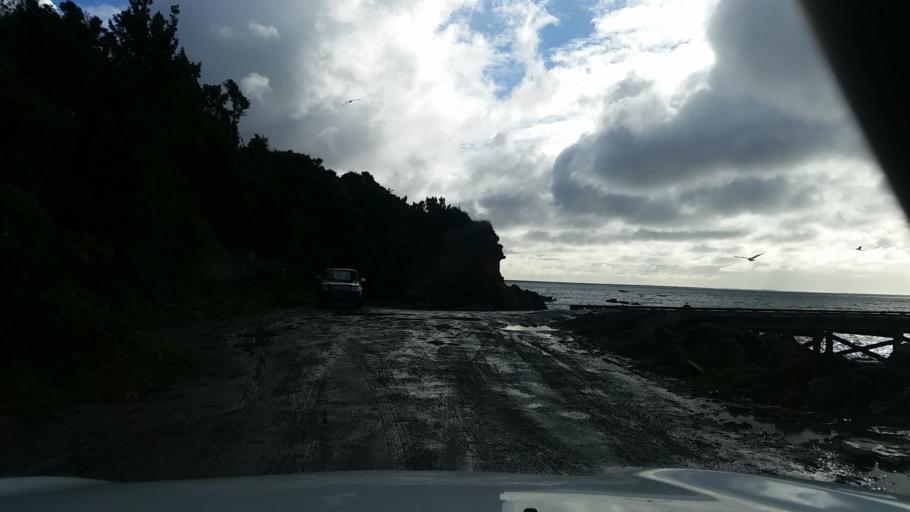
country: NZ
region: Chatham Islands
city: Waitangi
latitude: -44.0250
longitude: -176.3675
